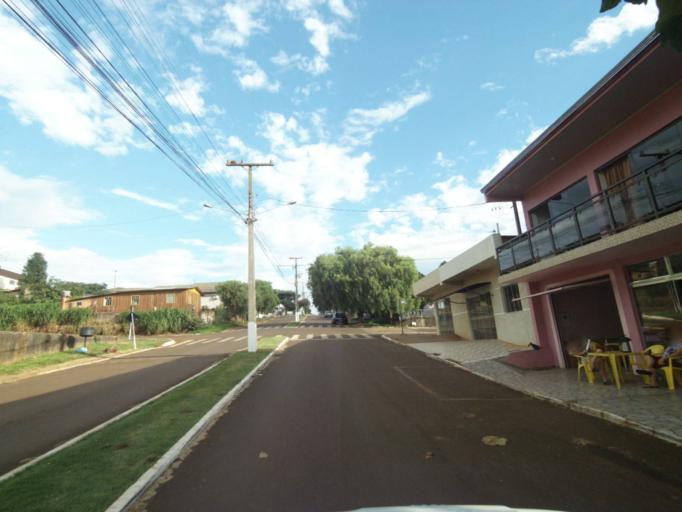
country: BR
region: Parana
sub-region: Laranjeiras Do Sul
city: Laranjeiras do Sul
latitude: -25.4889
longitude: -52.5266
